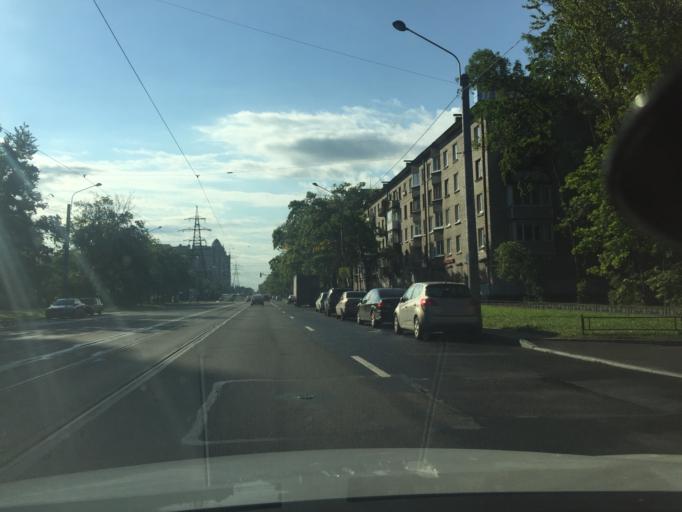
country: RU
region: St.-Petersburg
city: Kupchino
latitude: 59.8370
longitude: 30.3413
